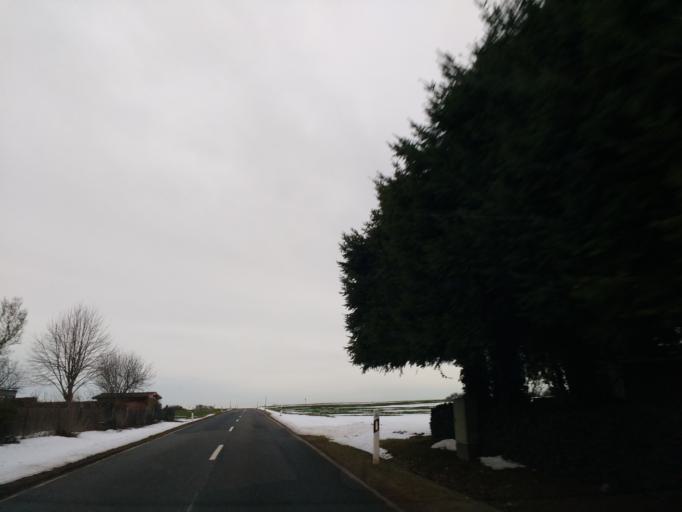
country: DE
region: Thuringia
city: Rohrberg
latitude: 51.4286
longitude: 10.0075
